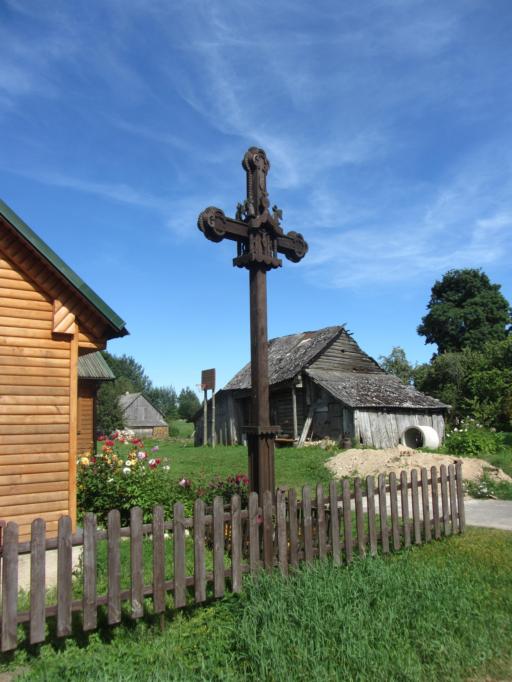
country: LT
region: Utenos apskritis
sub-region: Utena
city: Utena
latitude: 55.6877
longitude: 25.4147
